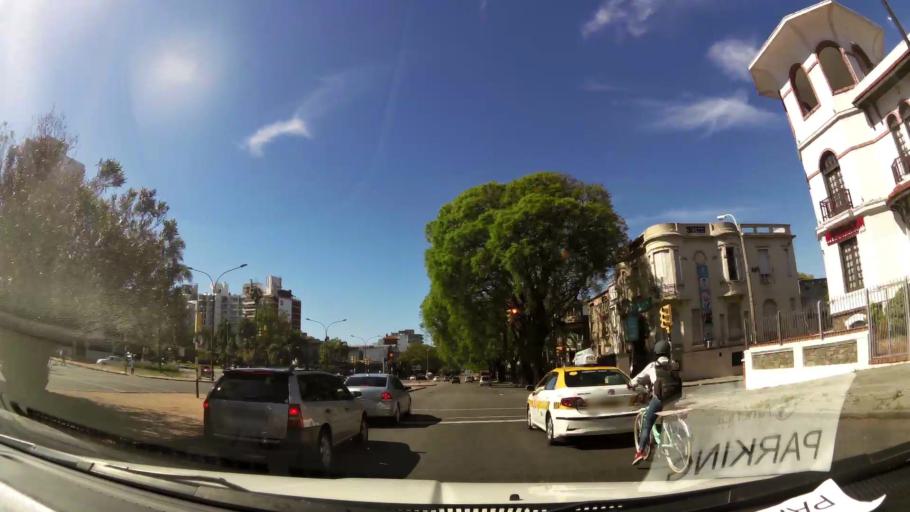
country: UY
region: Montevideo
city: Montevideo
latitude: -34.9054
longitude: -56.1639
